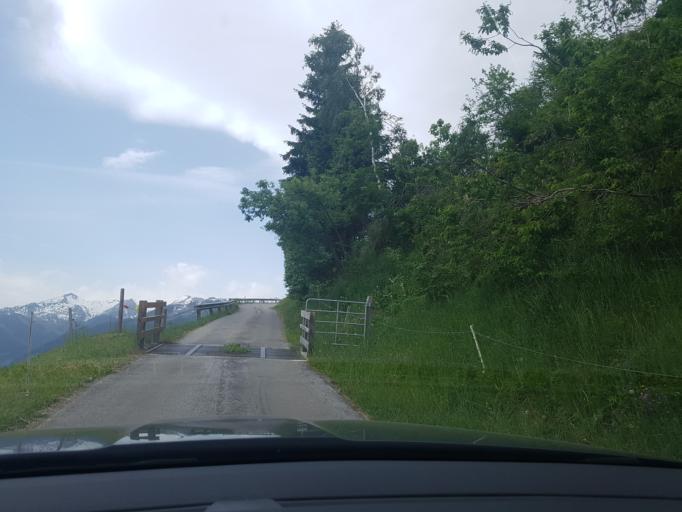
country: AT
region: Salzburg
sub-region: Politischer Bezirk Sankt Johann im Pongau
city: Schwarzach im Pongau
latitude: 47.2766
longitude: 13.2059
